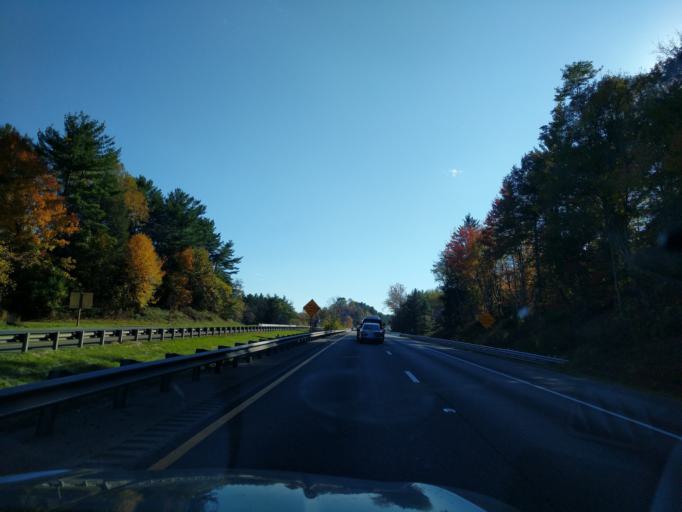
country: US
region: Virginia
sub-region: Pulaski County
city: Pulaski
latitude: 37.0277
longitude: -80.7293
